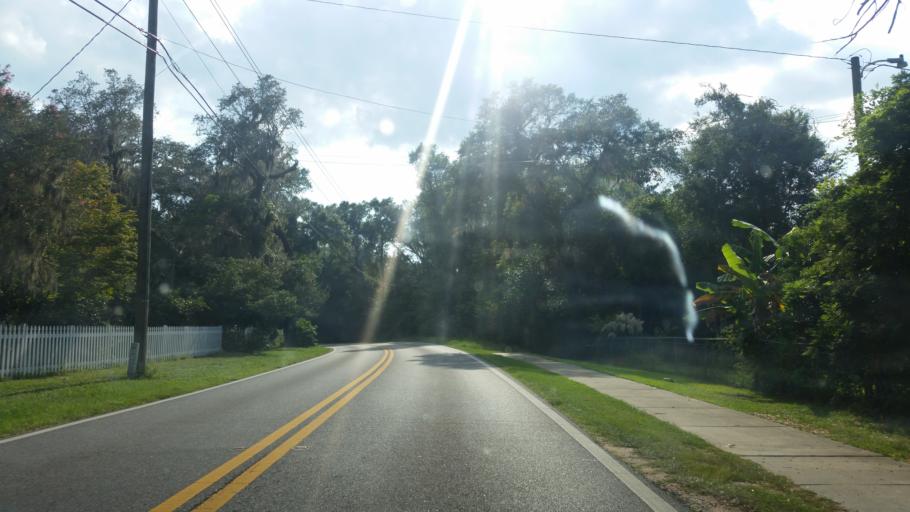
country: US
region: Florida
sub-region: Santa Rosa County
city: Bagdad
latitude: 30.6036
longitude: -87.0370
